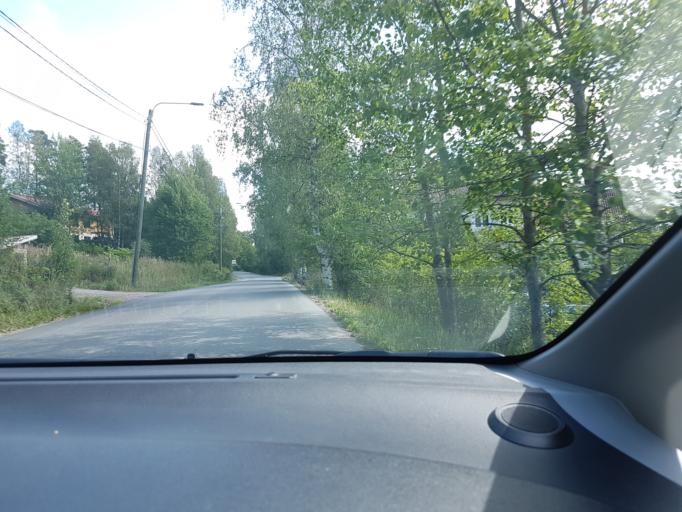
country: FI
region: Uusimaa
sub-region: Helsinki
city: Kilo
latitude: 60.3392
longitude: 24.8066
